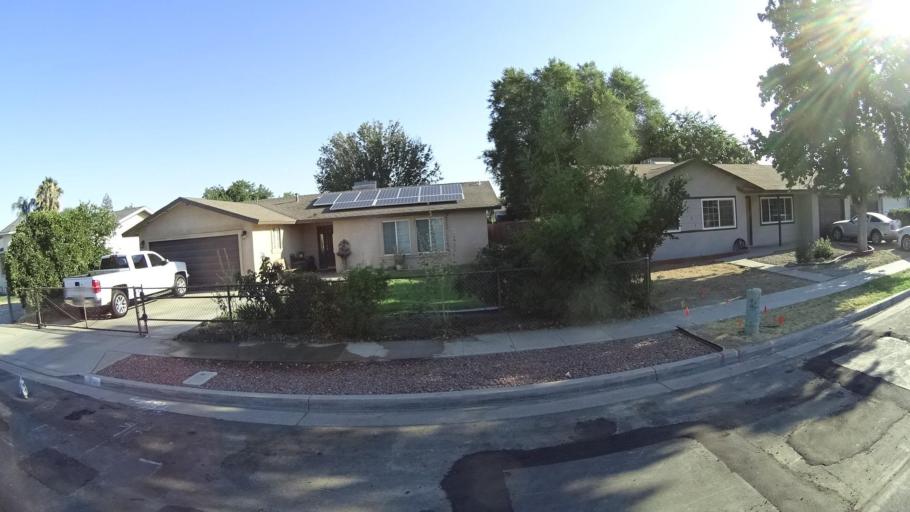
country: US
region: California
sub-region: Fresno County
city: Fresno
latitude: 36.7109
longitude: -119.7395
